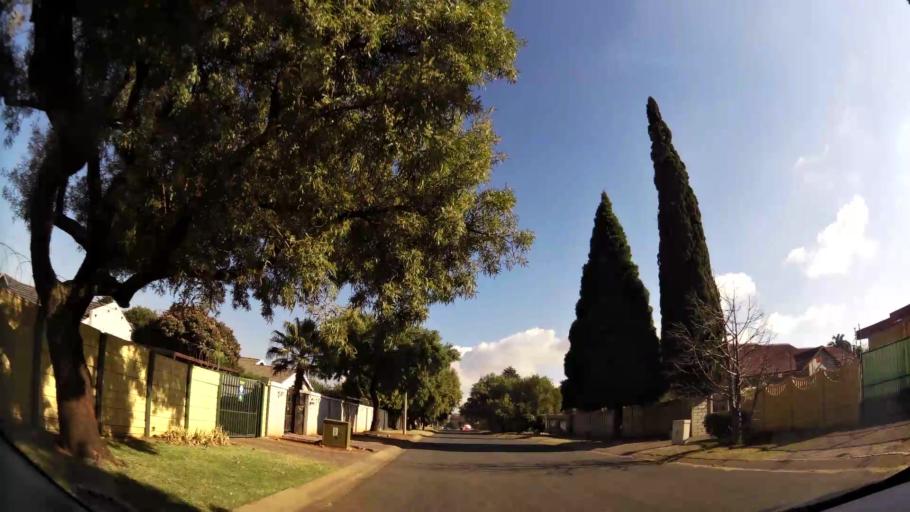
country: ZA
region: Gauteng
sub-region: City of Johannesburg Metropolitan Municipality
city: Roodepoort
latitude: -26.1599
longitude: 27.8229
